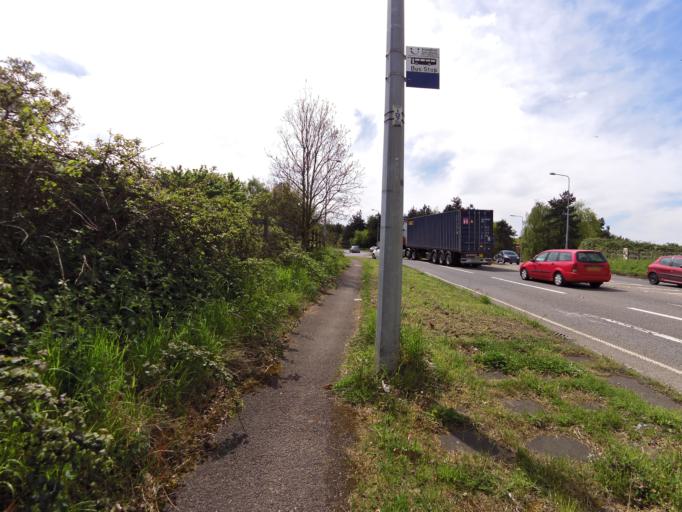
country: GB
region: England
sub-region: Suffolk
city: Ipswich
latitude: 52.0254
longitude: 1.1401
